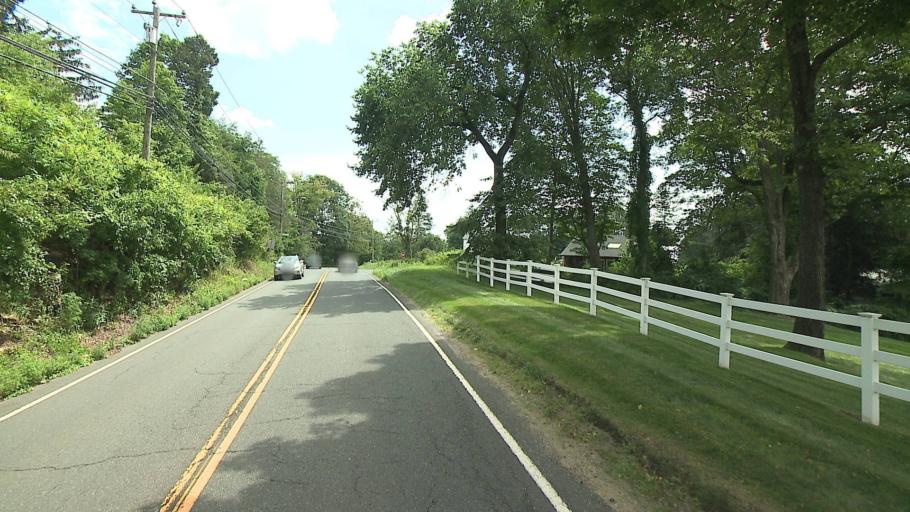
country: US
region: Connecticut
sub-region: Fairfield County
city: Danbury
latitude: 41.4217
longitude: -73.4799
